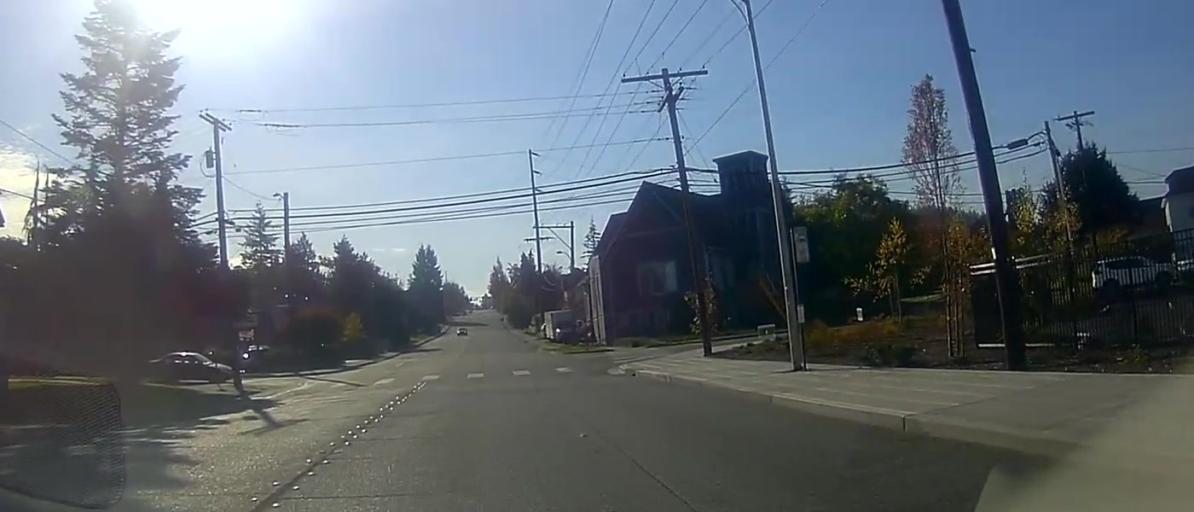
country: US
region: Washington
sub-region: Whatcom County
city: Bellingham
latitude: 48.7497
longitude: -122.4717
